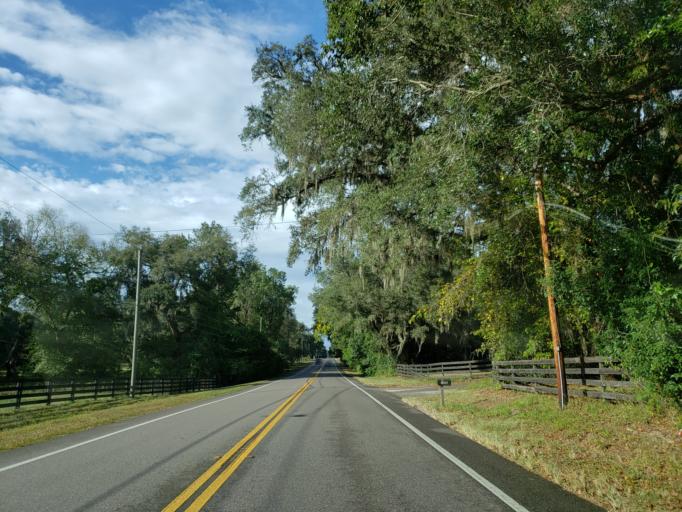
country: US
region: Florida
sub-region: Hernando County
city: Hill 'n Dale
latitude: 28.5092
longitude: -82.3030
